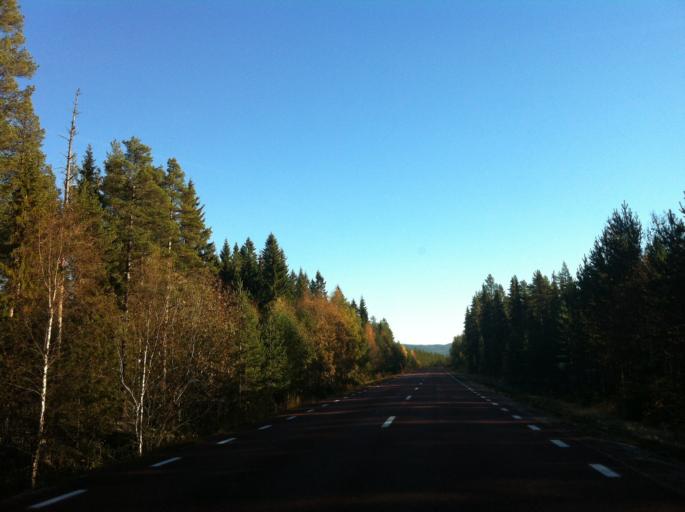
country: SE
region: Dalarna
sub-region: Alvdalens Kommun
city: AElvdalen
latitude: 61.3248
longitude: 13.6164
